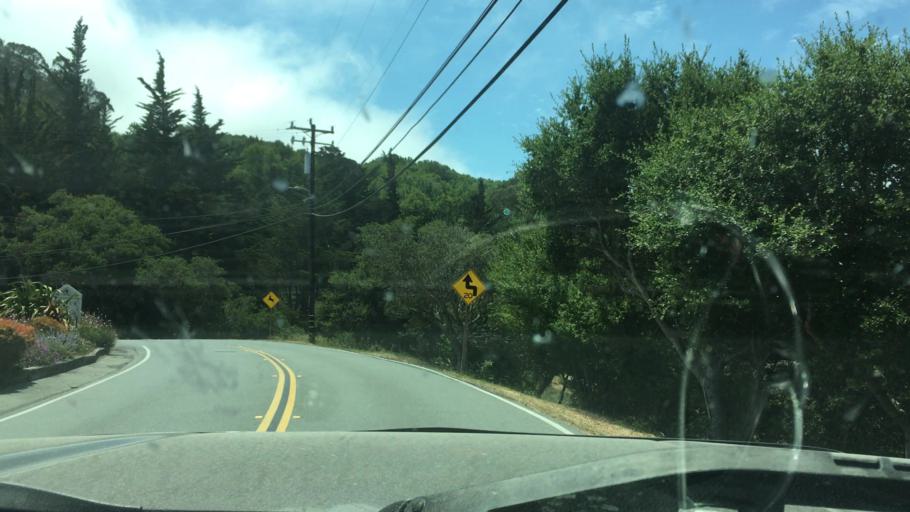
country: US
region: California
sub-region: Marin County
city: Tamalpais-Homestead Valley
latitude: 37.8791
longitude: -122.5233
